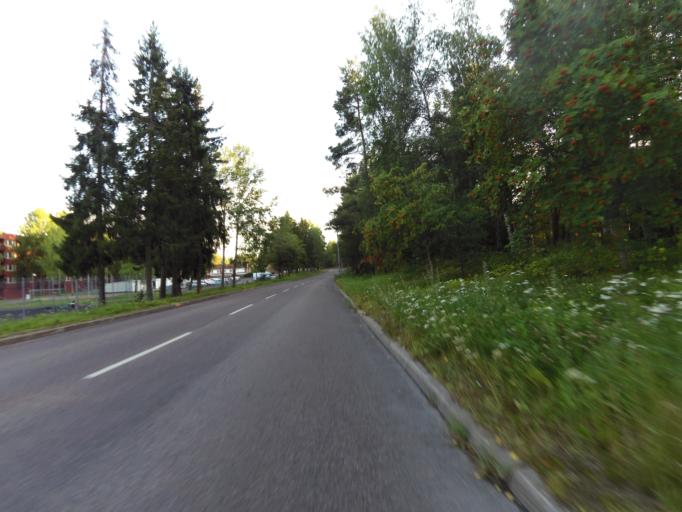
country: SE
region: Gaevleborg
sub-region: Gavle Kommun
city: Gavle
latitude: 60.6512
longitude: 17.1316
